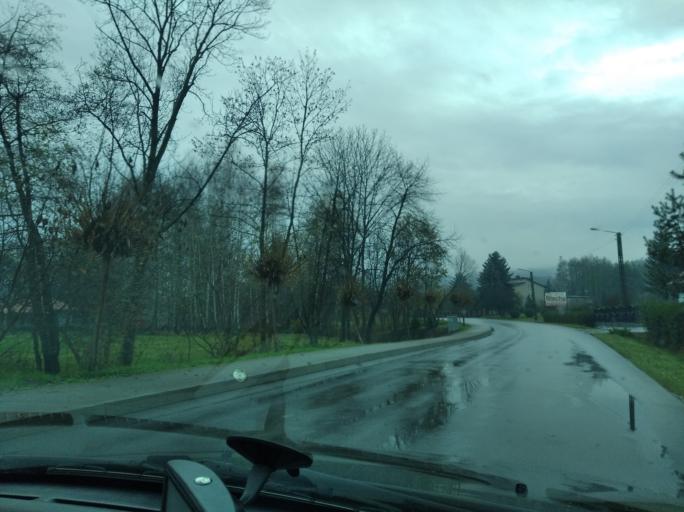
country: PL
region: Subcarpathian Voivodeship
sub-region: Powiat rzeszowski
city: Lubenia
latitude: 49.9272
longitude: 21.9270
